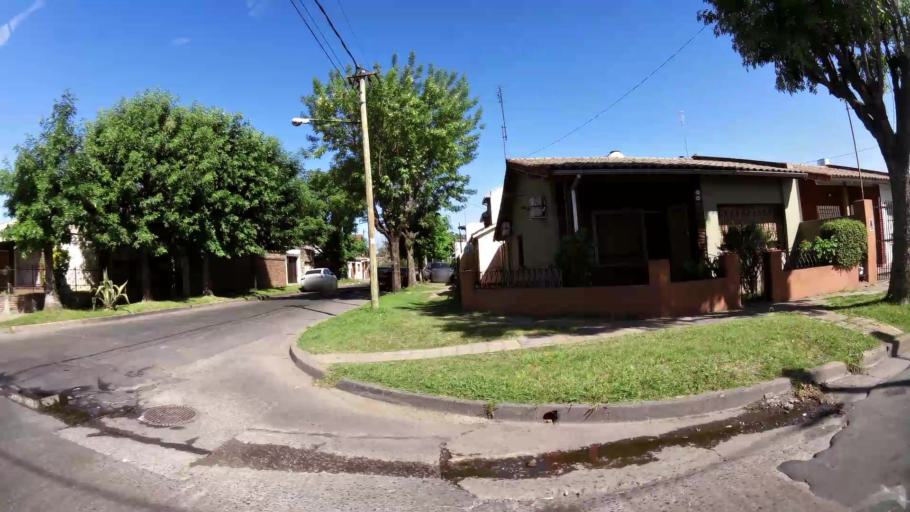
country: AR
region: Buenos Aires
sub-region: Partido de San Isidro
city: San Isidro
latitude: -34.5109
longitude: -58.5750
